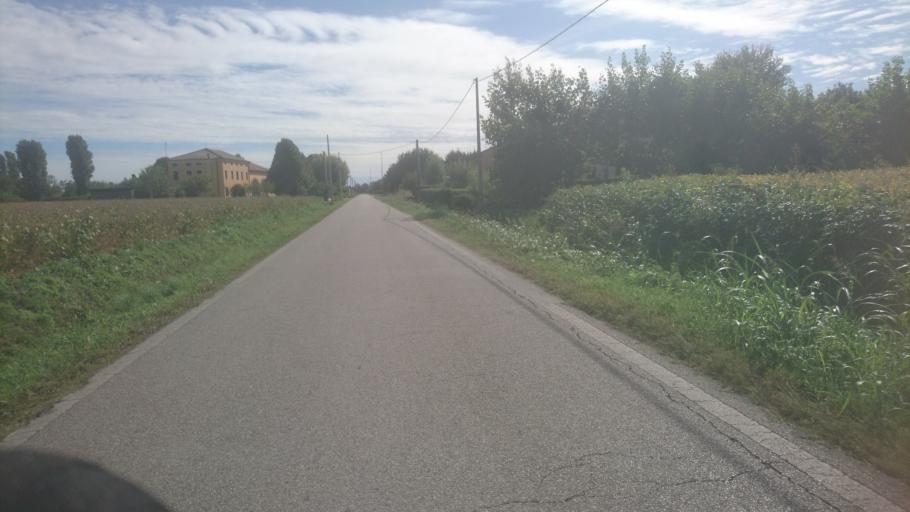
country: IT
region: Veneto
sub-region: Provincia di Padova
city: Veggiano
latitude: 45.4380
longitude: 11.7035
